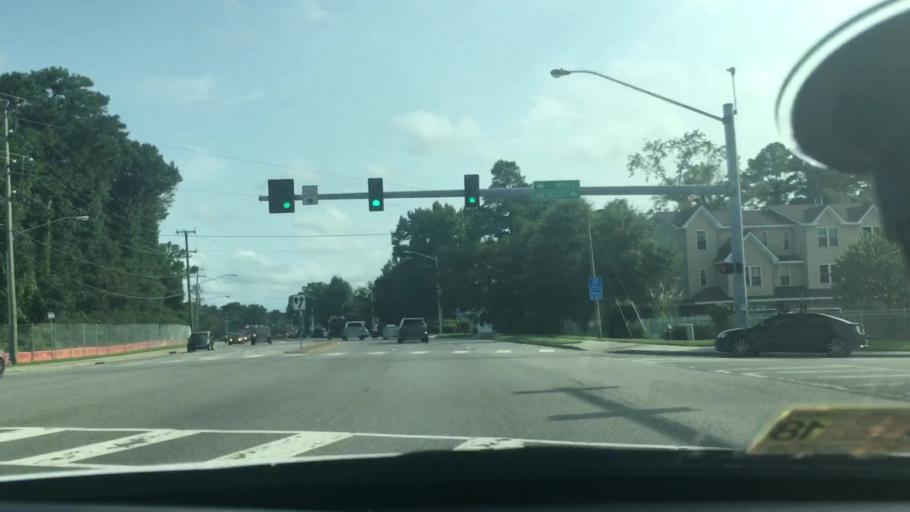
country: US
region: Virginia
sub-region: City of Virginia Beach
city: Virginia Beach
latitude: 36.8446
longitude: -75.9959
